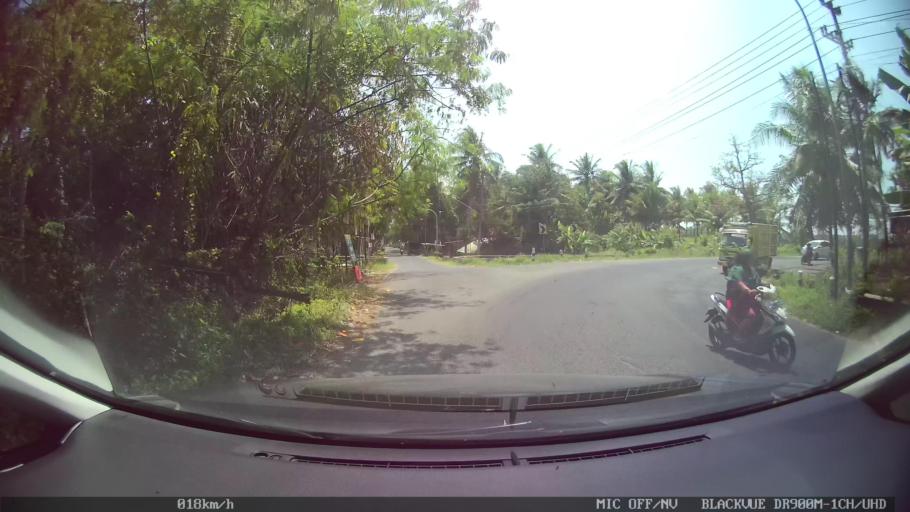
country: ID
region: Daerah Istimewa Yogyakarta
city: Srandakan
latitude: -7.9285
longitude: 110.1328
